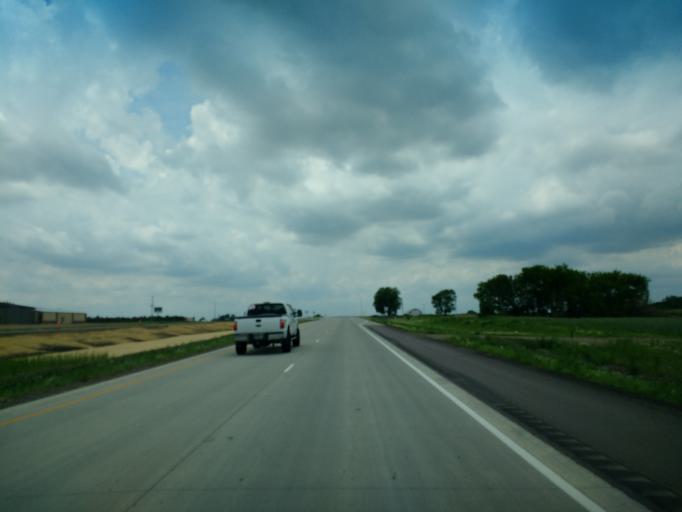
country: US
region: Minnesota
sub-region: Cottonwood County
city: Windom
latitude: 43.9102
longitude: -95.0453
